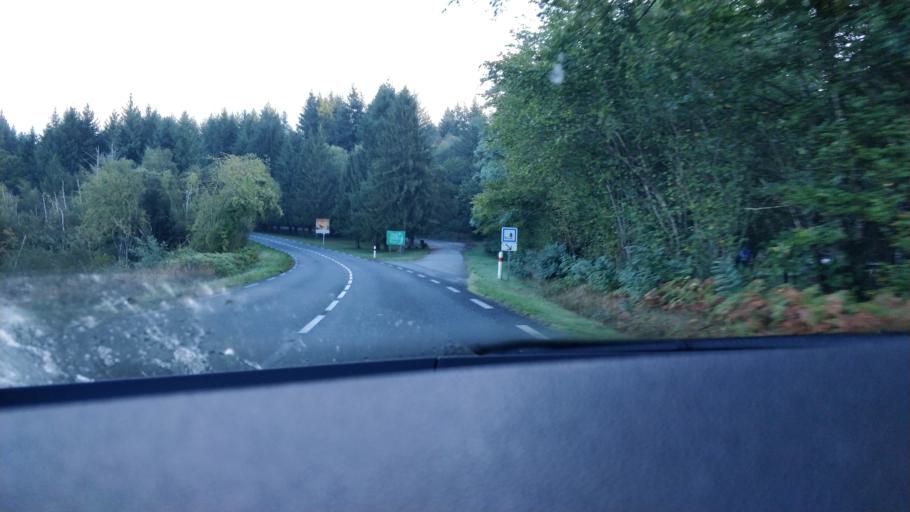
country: FR
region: Limousin
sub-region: Departement de la Haute-Vienne
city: Sauviat-sur-Vige
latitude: 45.9253
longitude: 1.6477
